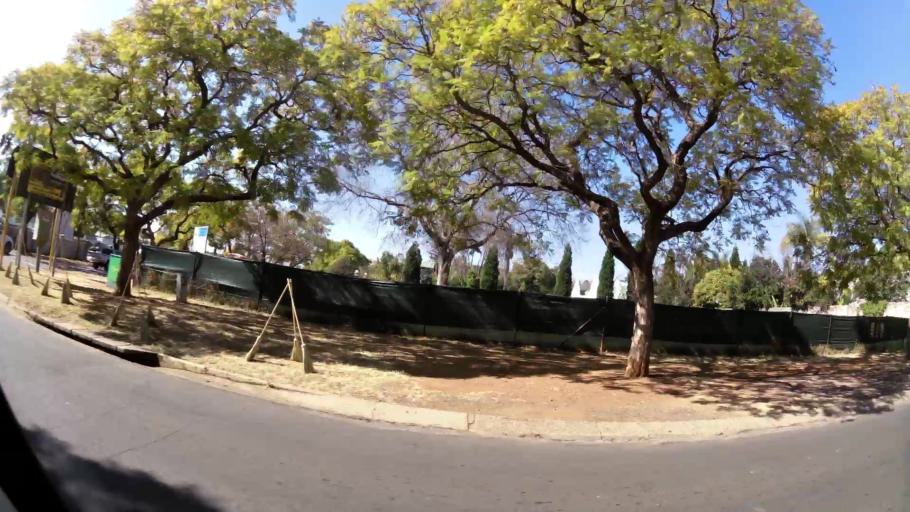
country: ZA
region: Gauteng
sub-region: City of Tshwane Metropolitan Municipality
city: Pretoria
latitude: -25.7689
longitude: 28.2431
